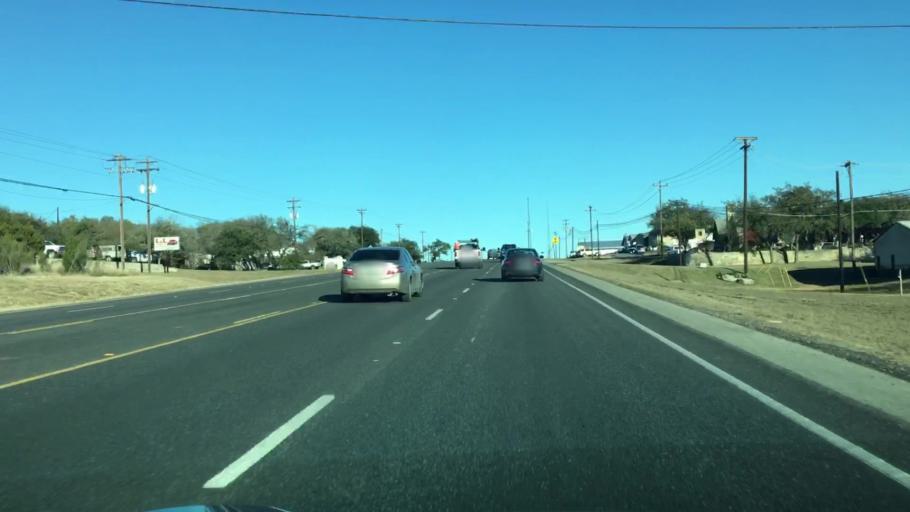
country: US
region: Texas
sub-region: Hays County
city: Dripping Springs
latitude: 30.1955
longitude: -98.0249
